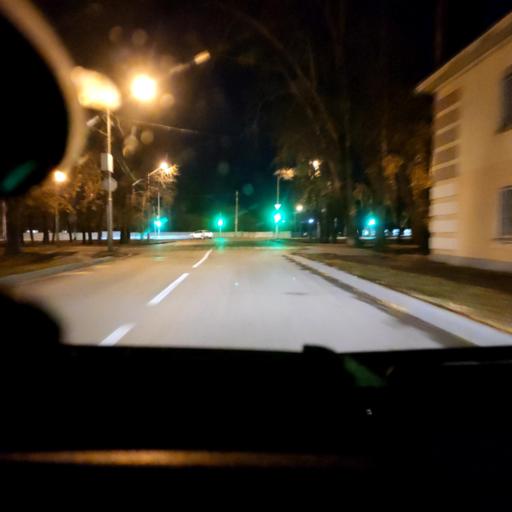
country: RU
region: Bashkortostan
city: Mikhaylovka
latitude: 54.7012
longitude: 55.8385
